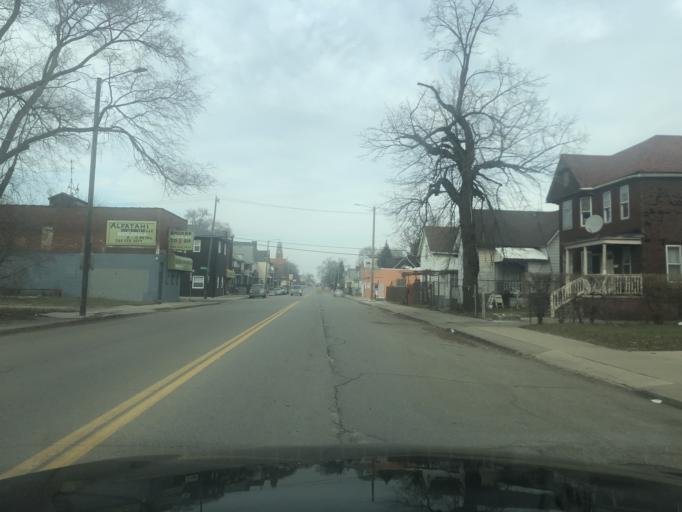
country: US
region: Michigan
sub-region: Wayne County
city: River Rouge
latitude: 42.3134
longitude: -83.0986
